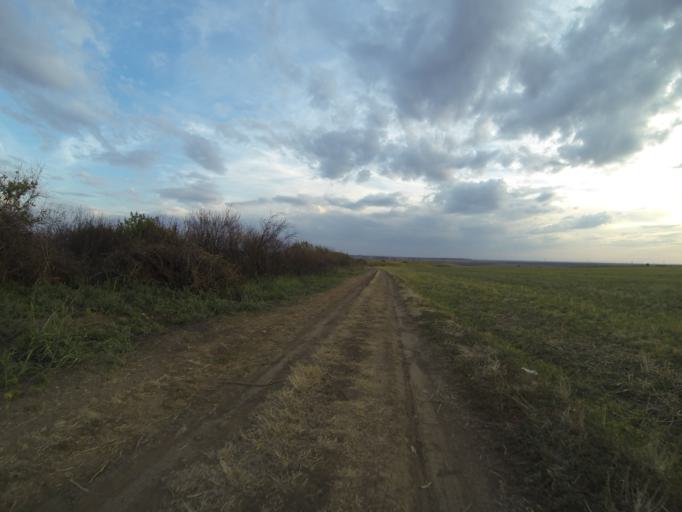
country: RO
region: Dolj
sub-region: Comuna Ceratu
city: Ceratu
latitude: 44.1012
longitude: 23.6711
